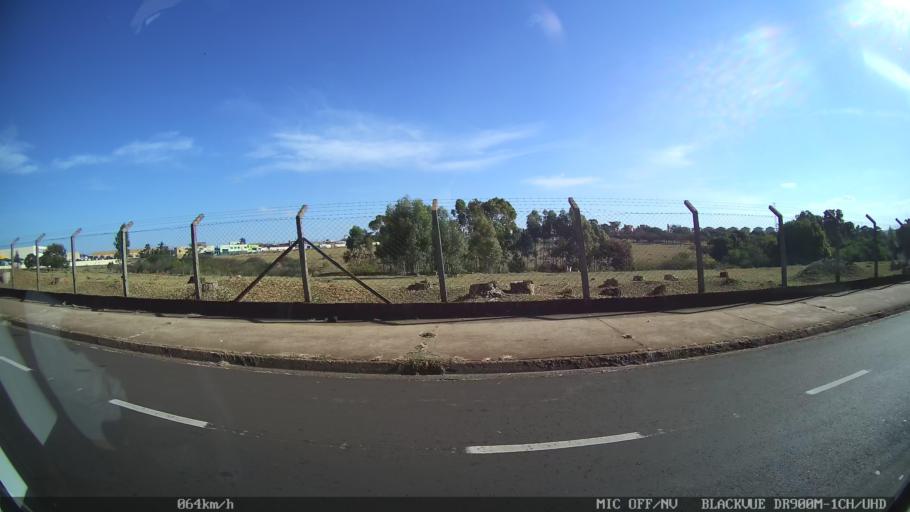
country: BR
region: Sao Paulo
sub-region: Franca
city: Franca
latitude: -20.5242
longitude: -47.4339
